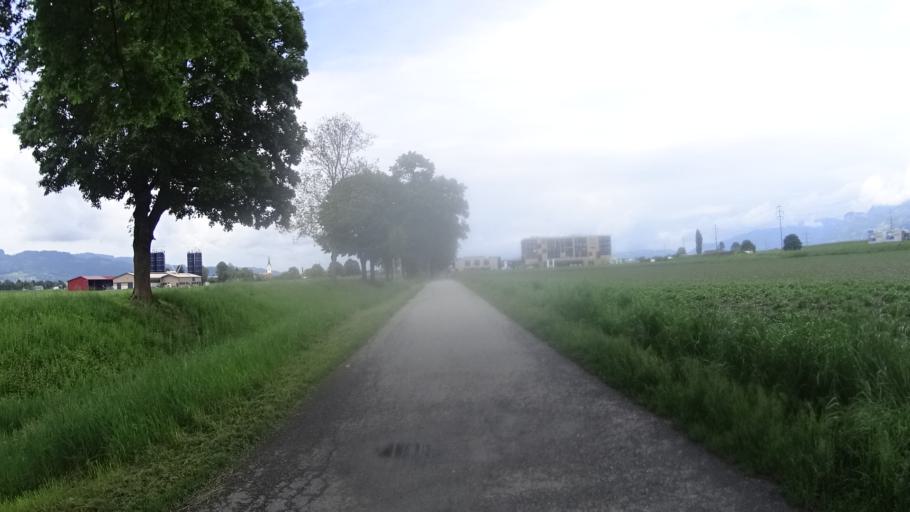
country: AT
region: Vorarlberg
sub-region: Politischer Bezirk Feldkirch
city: Mader
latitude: 47.3561
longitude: 9.6037
